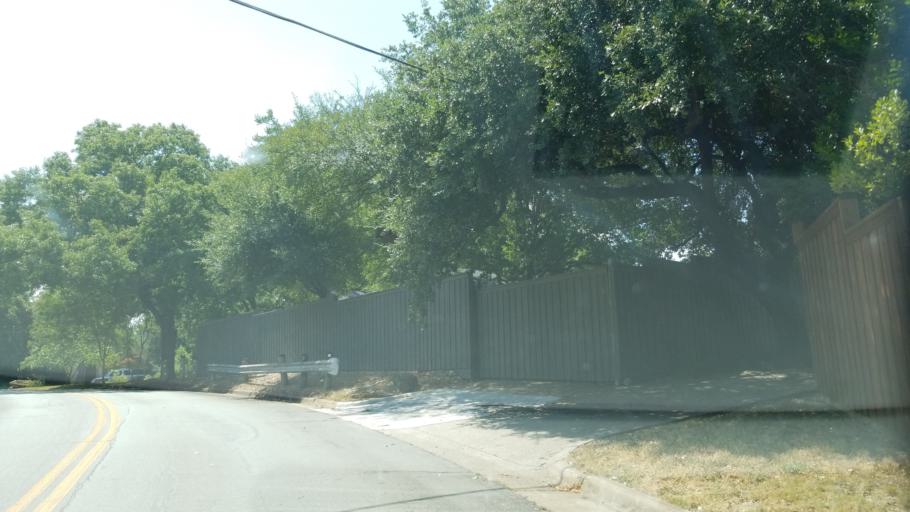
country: US
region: Texas
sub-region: Dallas County
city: Cockrell Hill
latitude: 32.7618
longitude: -96.8511
